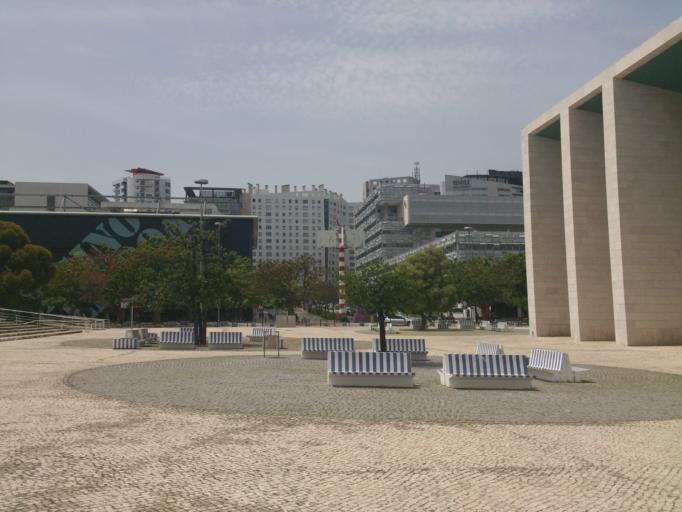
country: PT
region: Lisbon
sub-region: Loures
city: Moscavide
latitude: 38.7653
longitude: -9.0949
